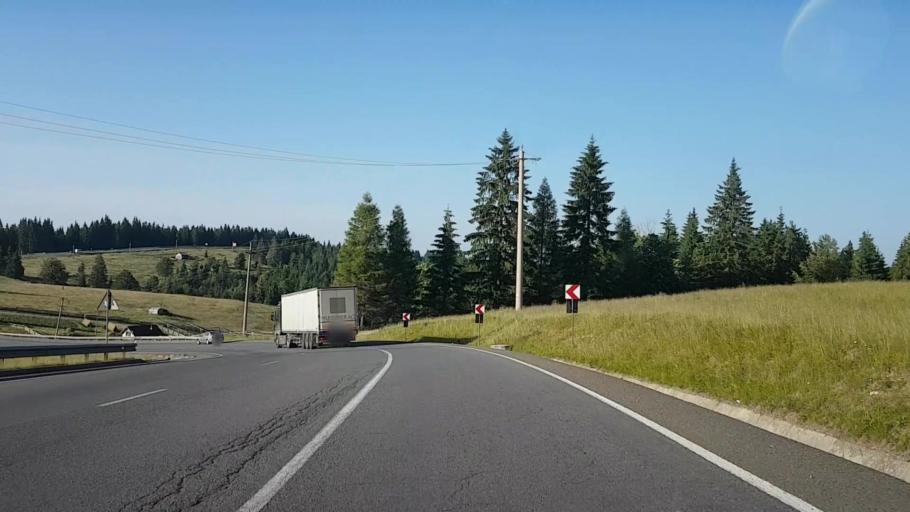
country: RO
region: Bistrita-Nasaud
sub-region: Comuna Lunca Ilvei
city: Lunca Ilvei
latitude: 47.2736
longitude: 25.0281
